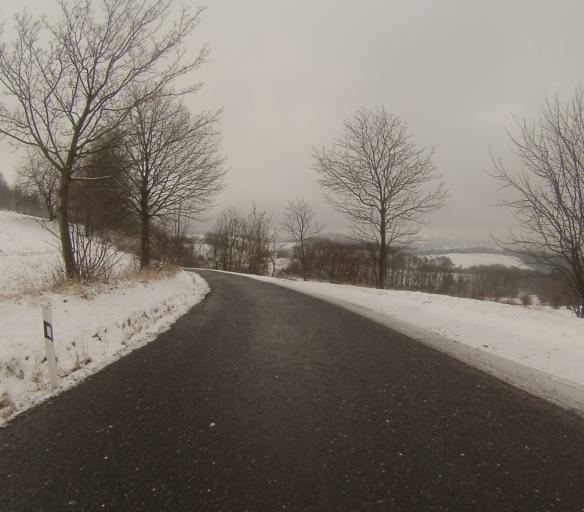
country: CZ
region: Ustecky
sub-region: Okres Decin
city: Decin
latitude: 50.7295
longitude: 14.2411
